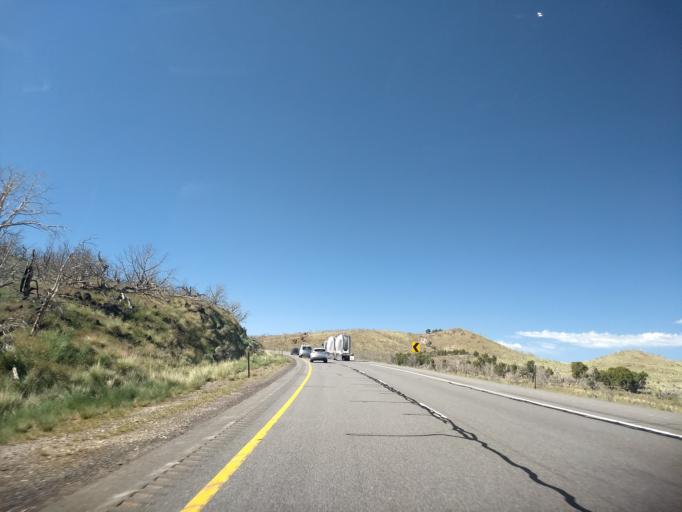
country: US
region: Utah
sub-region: Beaver County
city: Beaver
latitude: 38.6291
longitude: -112.6081
